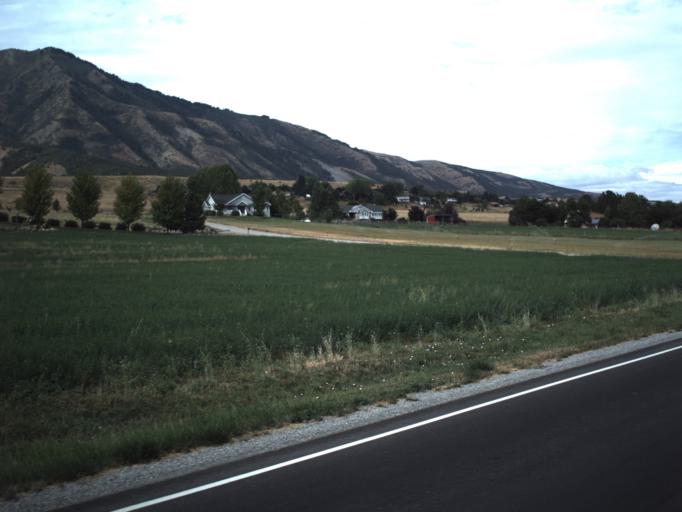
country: US
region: Utah
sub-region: Cache County
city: Mendon
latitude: 41.6846
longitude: -111.9646
